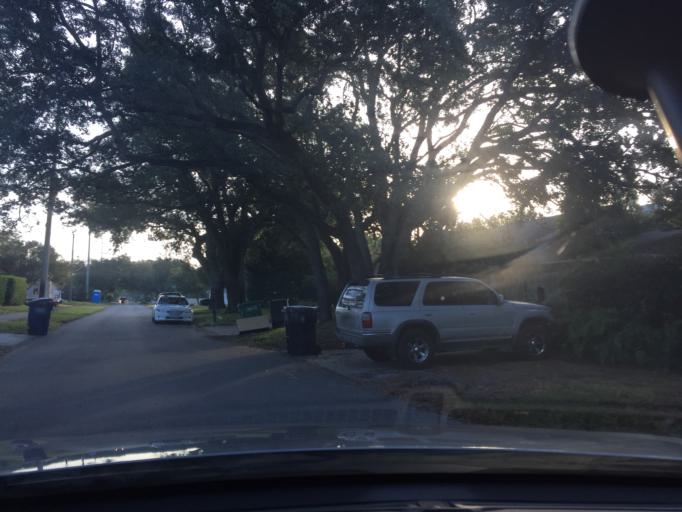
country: US
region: Florida
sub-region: Hillsborough County
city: Tampa
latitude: 27.9510
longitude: -82.4973
